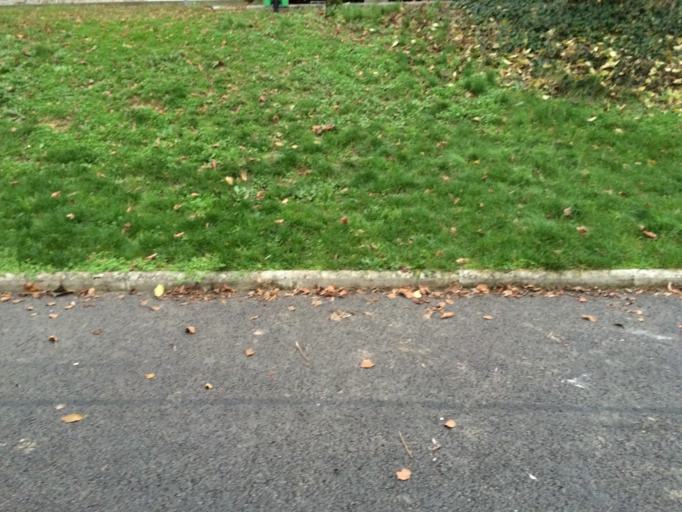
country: FR
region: Pays de la Loire
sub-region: Departement de la Vendee
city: Chaille-les-Marais
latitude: 46.3927
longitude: -1.0214
